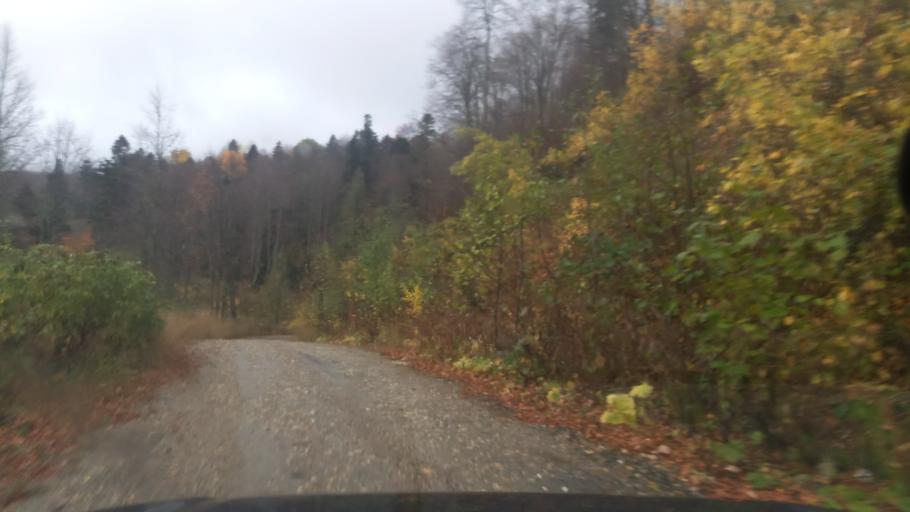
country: RU
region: Krasnodarskiy
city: Dagomys
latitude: 43.9920
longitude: 39.8544
